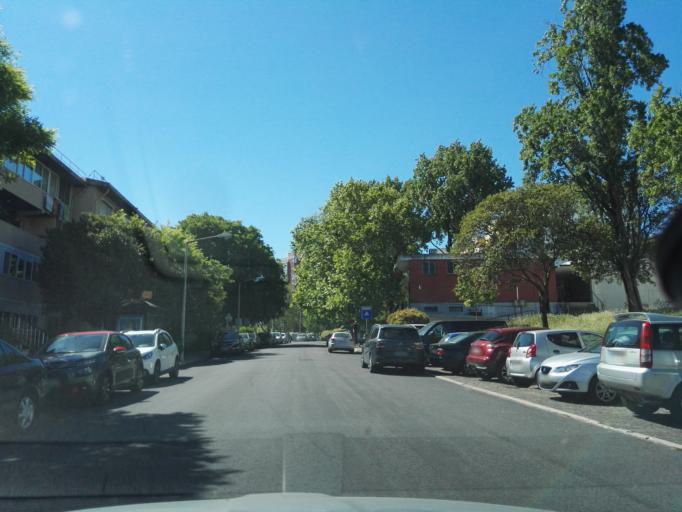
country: PT
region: Lisbon
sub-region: Loures
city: Moscavide
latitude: 38.7657
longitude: -9.1111
